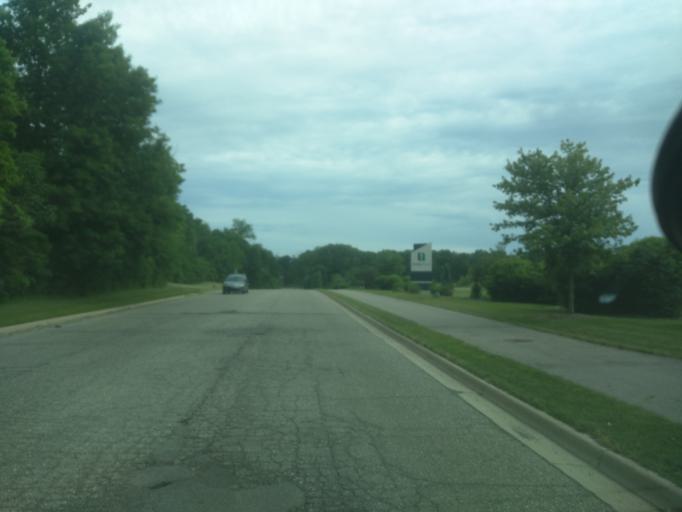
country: US
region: Michigan
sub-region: Ingham County
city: Holt
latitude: 42.6790
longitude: -84.5138
